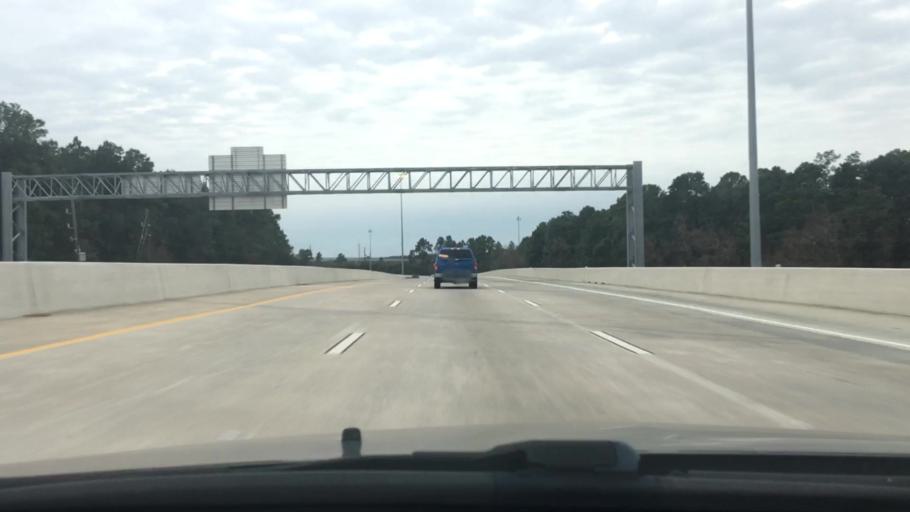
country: US
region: Texas
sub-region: Harris County
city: Spring
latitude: 30.0745
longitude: -95.4116
